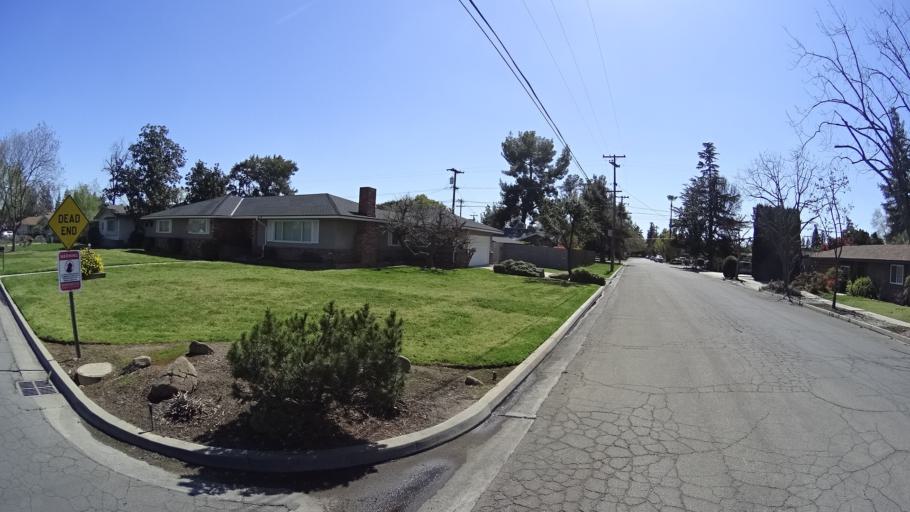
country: US
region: California
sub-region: Fresno County
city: Fresno
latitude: 36.8202
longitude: -119.8015
